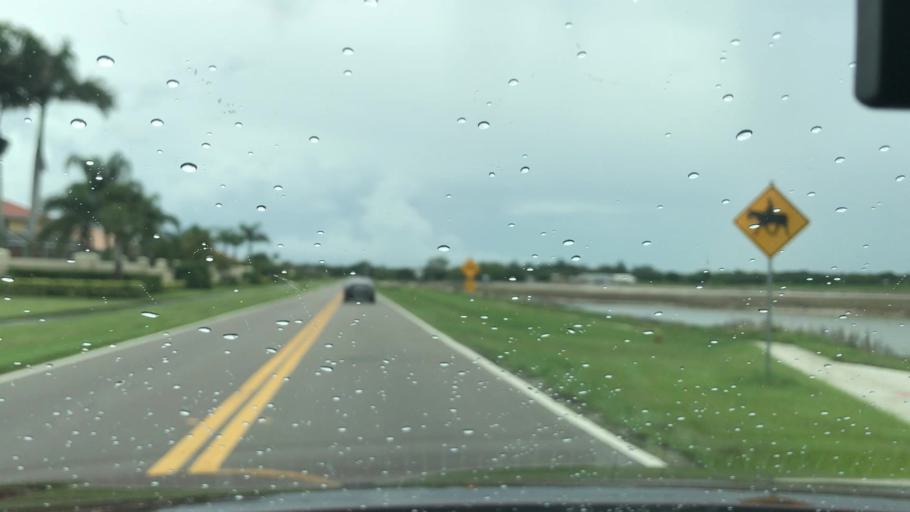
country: US
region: Florida
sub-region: Sarasota County
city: Lake Sarasota
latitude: 27.3128
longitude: -82.3928
